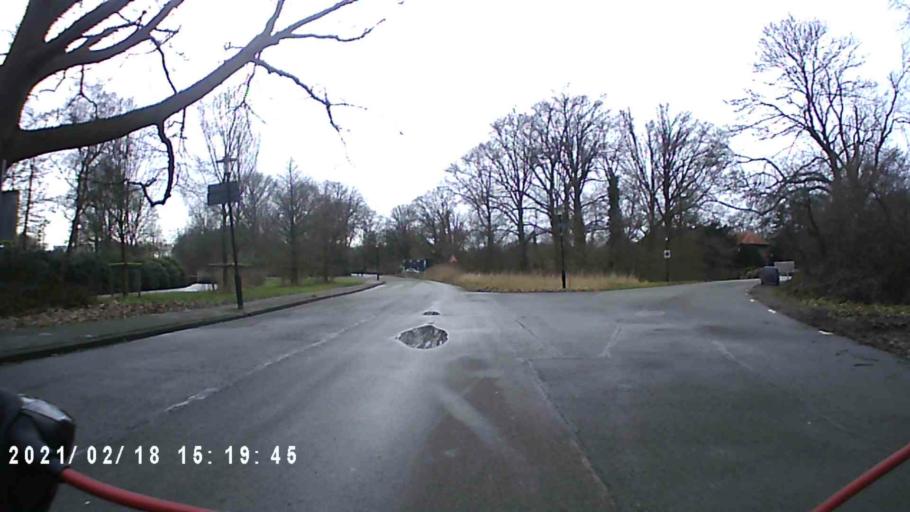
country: NL
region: Groningen
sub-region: Gemeente Groningen
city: Groningen
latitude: 53.2006
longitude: 6.5465
